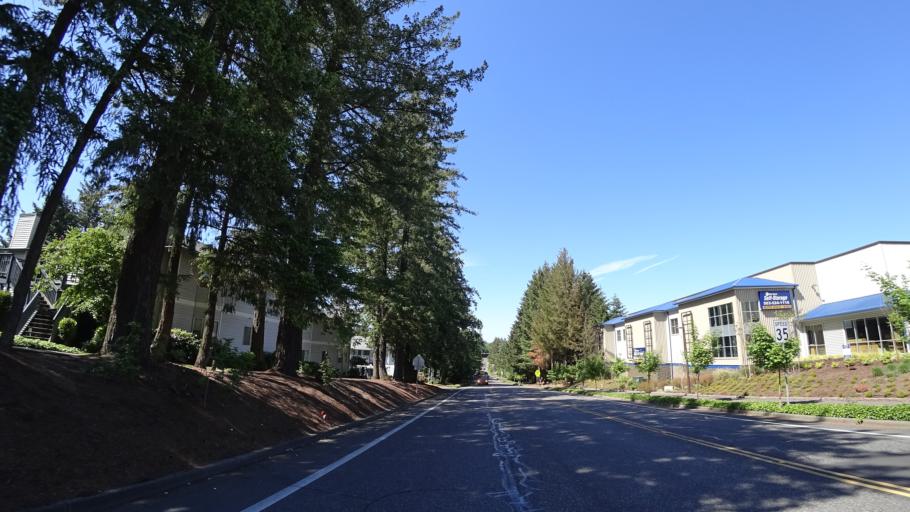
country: US
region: Oregon
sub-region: Washington County
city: Beaverton
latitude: 45.4513
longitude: -122.8055
